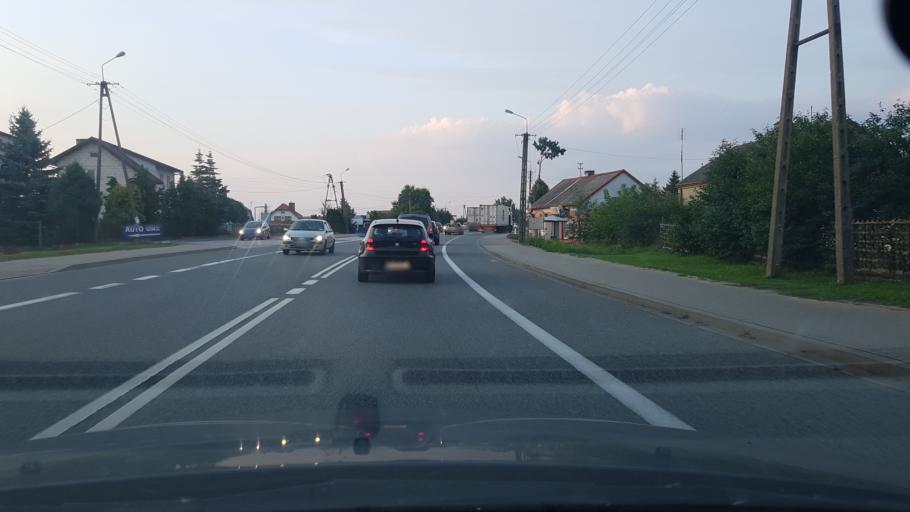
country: PL
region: Masovian Voivodeship
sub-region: Powiat mlawski
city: Mlawa
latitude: 53.1649
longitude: 20.4142
